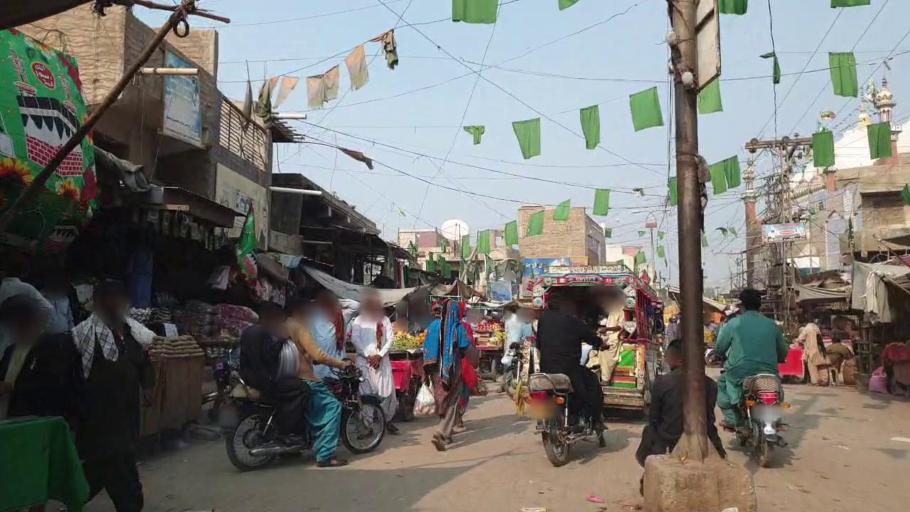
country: PK
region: Sindh
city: Bhan
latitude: 26.5579
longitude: 67.7207
